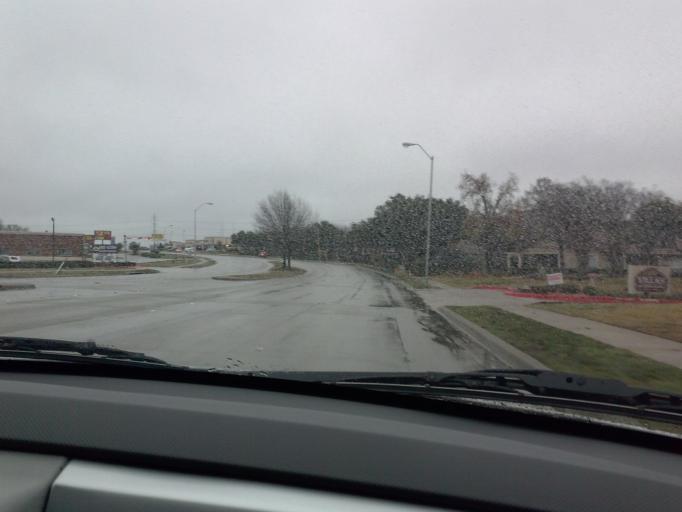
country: US
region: Texas
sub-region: Collin County
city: Allen
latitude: 33.0683
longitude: -96.7021
